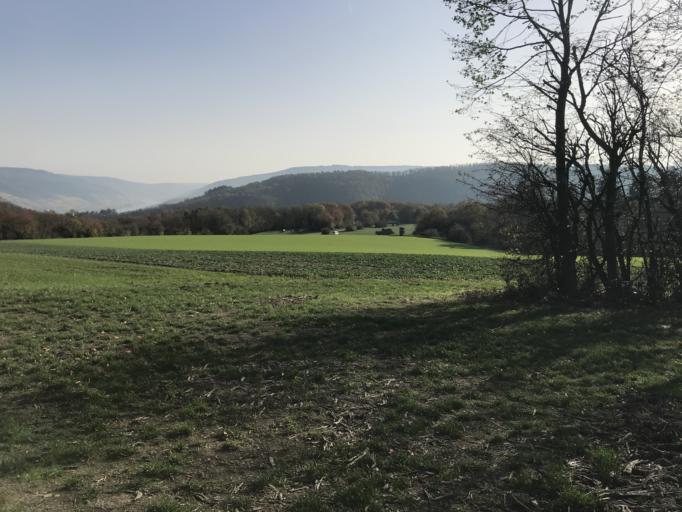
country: DE
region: Rheinland-Pfalz
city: Bacharach
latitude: 50.0629
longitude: 7.7447
